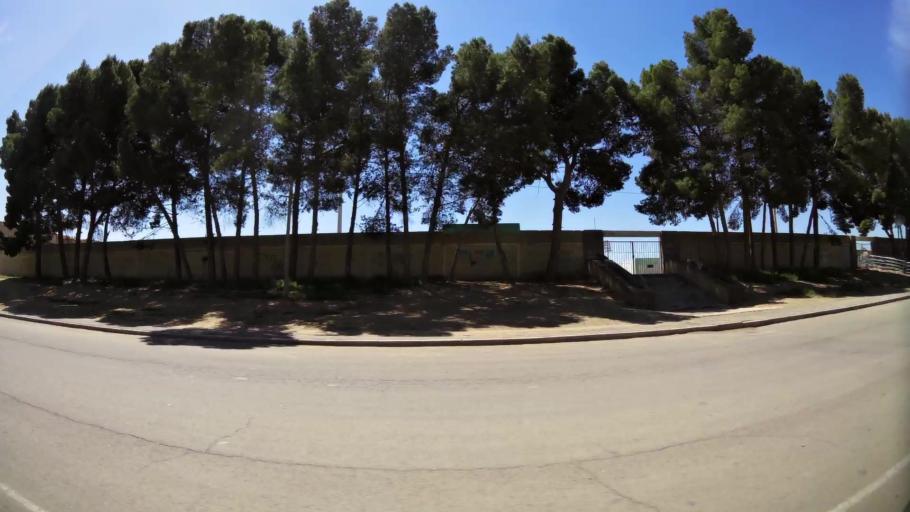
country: MA
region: Oriental
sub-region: Oujda-Angad
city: Oujda
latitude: 34.6612
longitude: -1.9347
